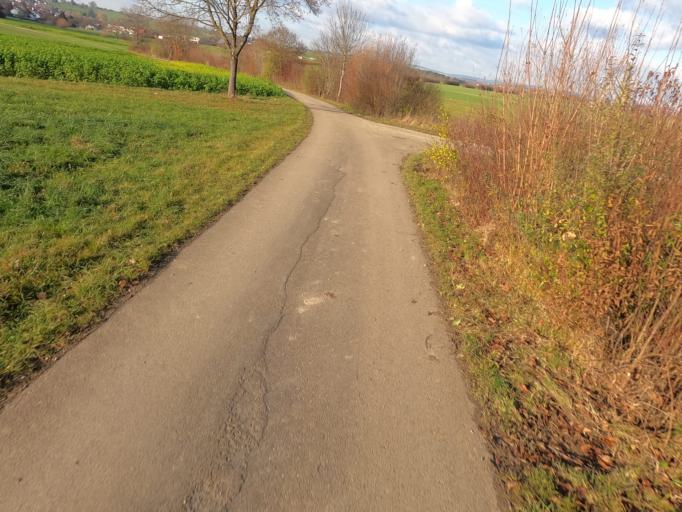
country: DE
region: Baden-Wuerttemberg
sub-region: Regierungsbezirk Stuttgart
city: Hattenhofen
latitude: 48.6654
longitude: 9.5898
